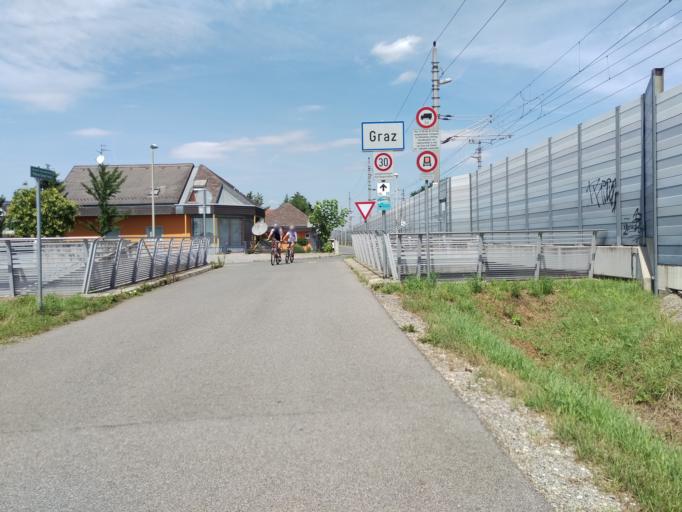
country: AT
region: Styria
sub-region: Politischer Bezirk Graz-Umgebung
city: Feldkirchen bei Graz
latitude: 47.0204
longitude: 15.4353
